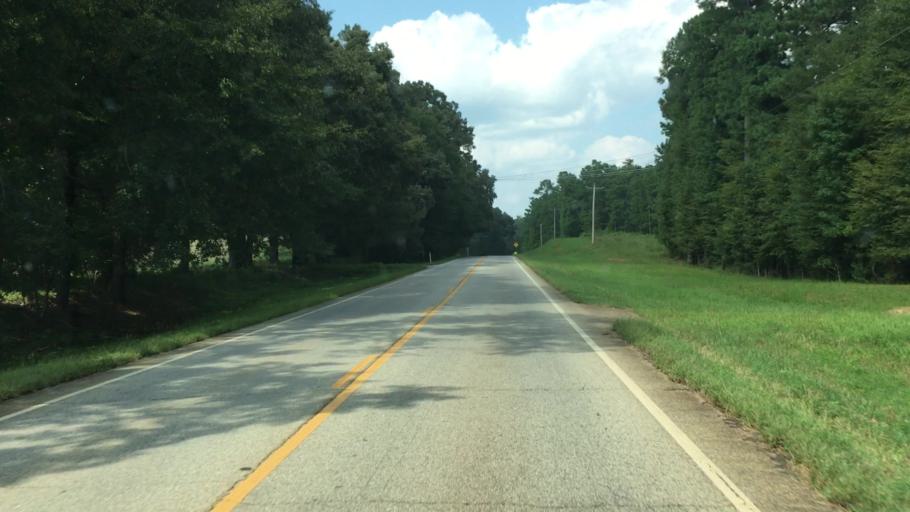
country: US
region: Georgia
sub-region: Butts County
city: Indian Springs
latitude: 33.1450
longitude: -83.8526
